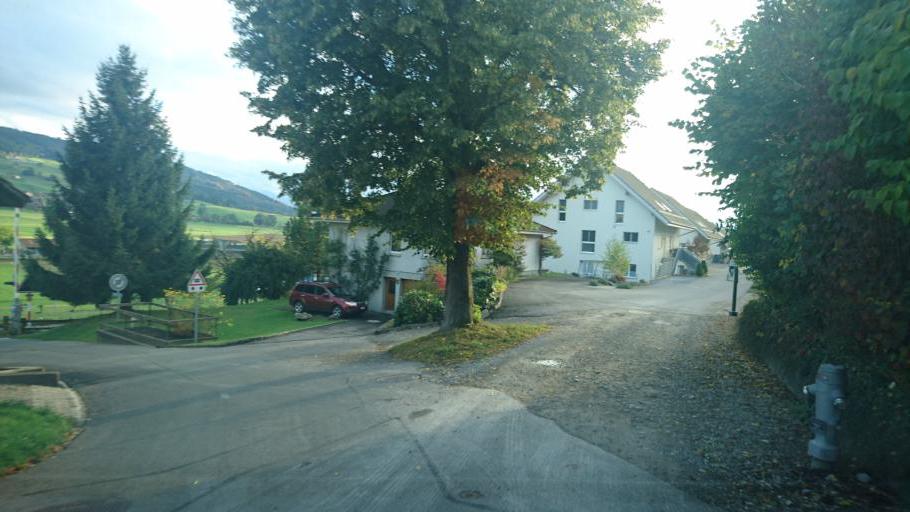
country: CH
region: Bern
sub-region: Bern-Mittelland District
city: Konolfingen
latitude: 46.8887
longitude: 7.6315
